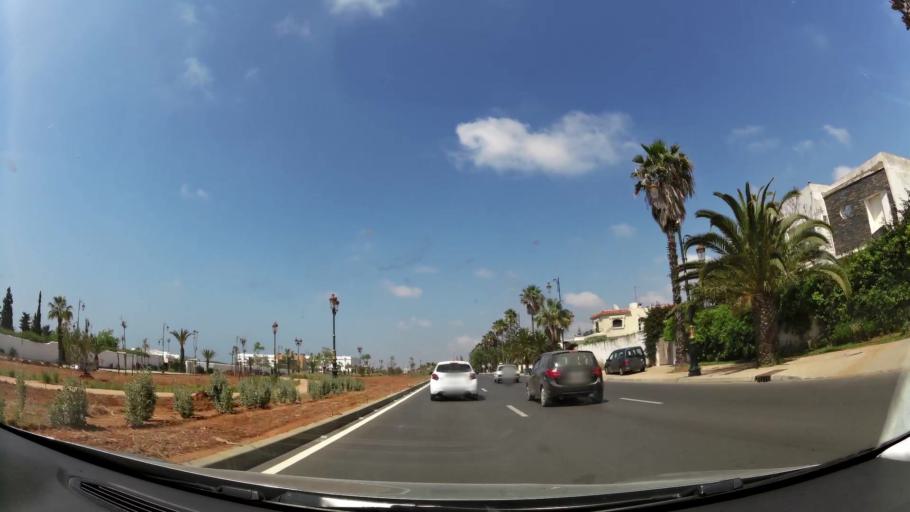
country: MA
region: Rabat-Sale-Zemmour-Zaer
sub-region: Skhirate-Temara
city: Temara
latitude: 33.9677
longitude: -6.8679
